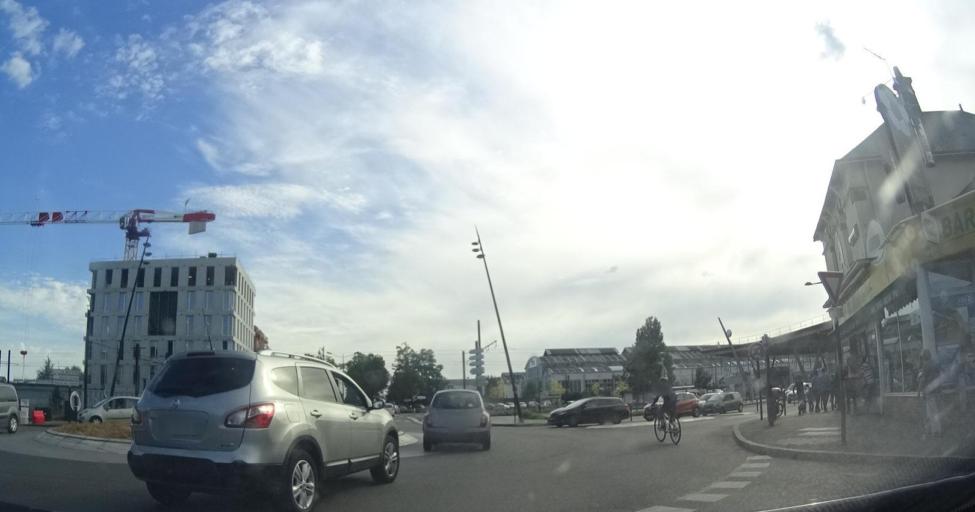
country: FR
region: Pays de la Loire
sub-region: Departement de la Loire-Atlantique
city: Sainte-Luce-sur-Loire
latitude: 47.2489
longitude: -1.5210
